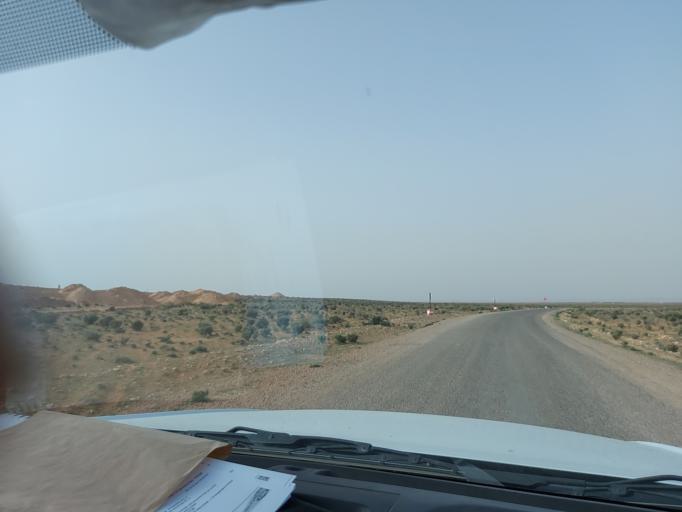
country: TN
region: Madanin
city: Medenine
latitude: 33.2867
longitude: 10.5993
